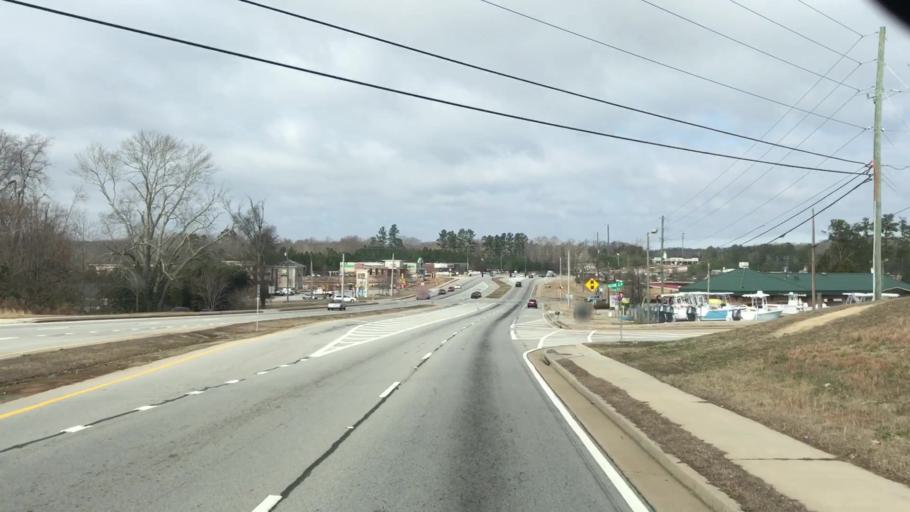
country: US
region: Georgia
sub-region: Hall County
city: Oakwood
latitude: 34.1919
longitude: -83.8578
